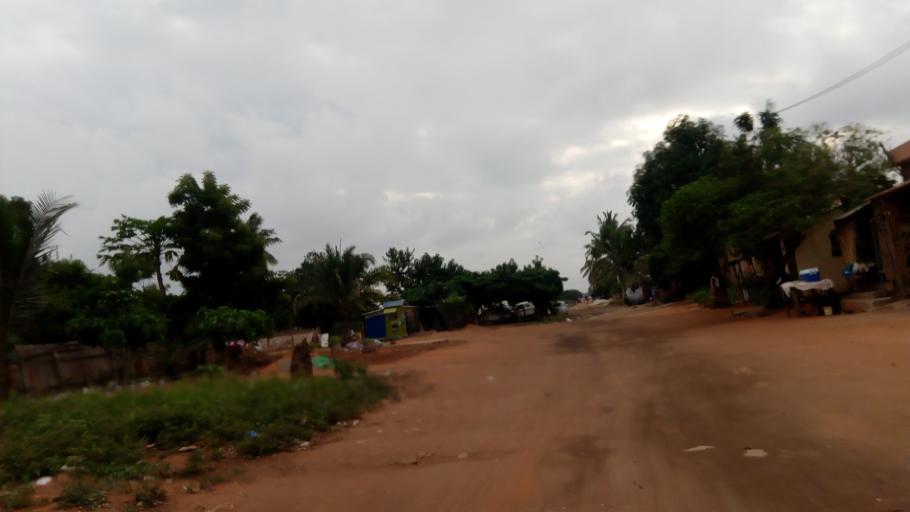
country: TG
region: Maritime
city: Lome
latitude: 6.1732
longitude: 1.1950
